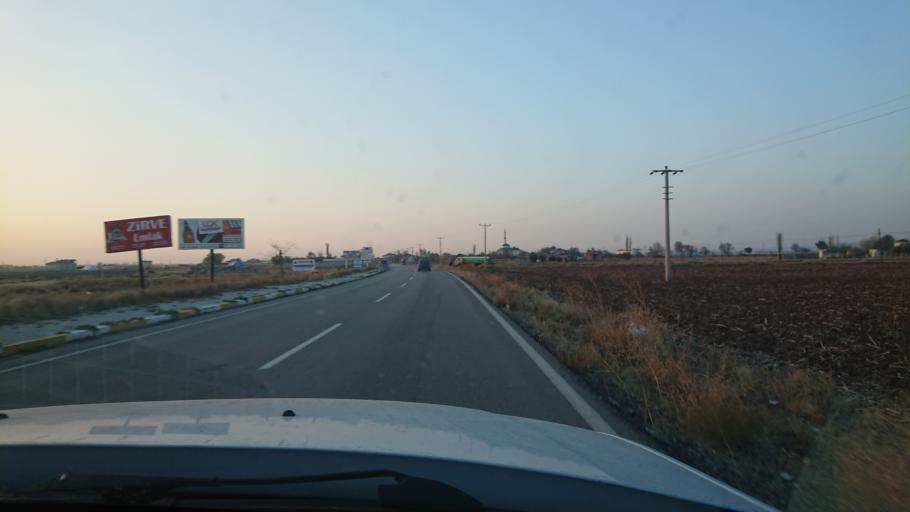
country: TR
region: Aksaray
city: Aksaray
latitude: 38.3143
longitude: 34.0583
